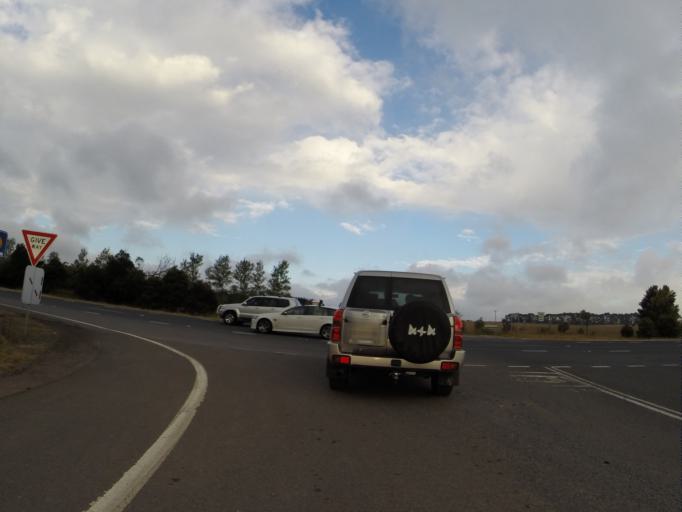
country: AU
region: New South Wales
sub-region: Wingecarribee
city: Moss Vale
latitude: -34.5365
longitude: 150.2806
